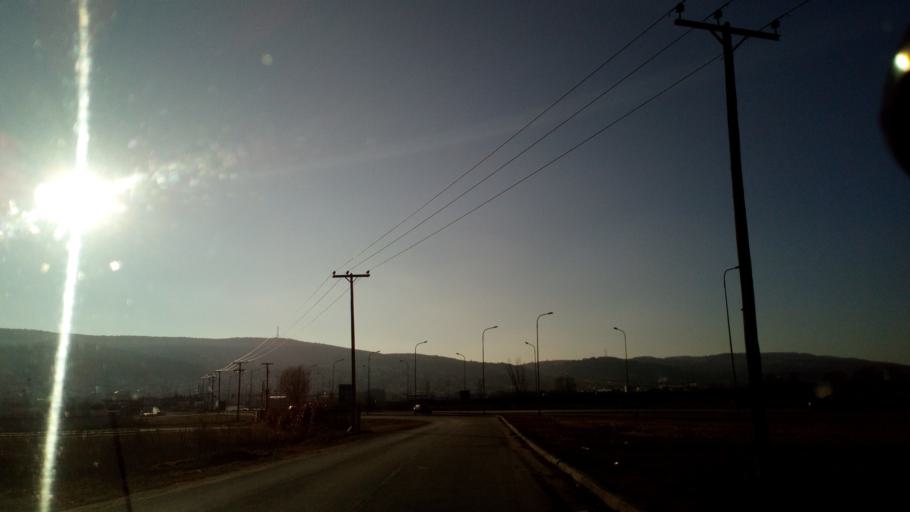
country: GR
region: Central Macedonia
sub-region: Nomos Thessalonikis
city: Lagyna
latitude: 40.7300
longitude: 23.0184
